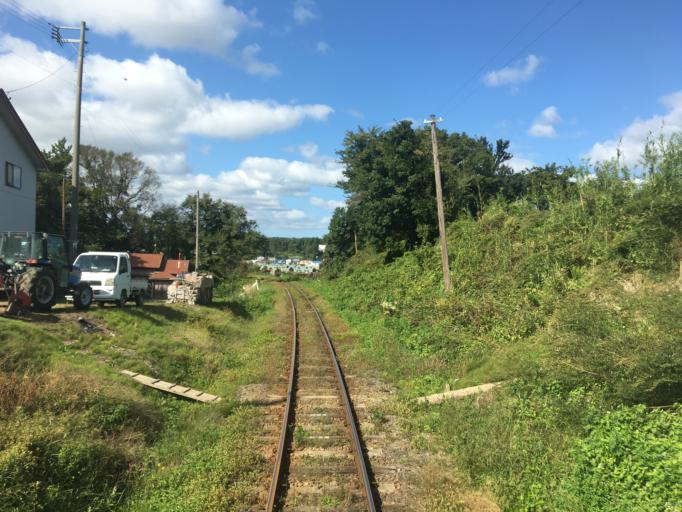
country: JP
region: Aomori
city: Goshogawara
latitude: 40.9591
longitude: 140.4436
